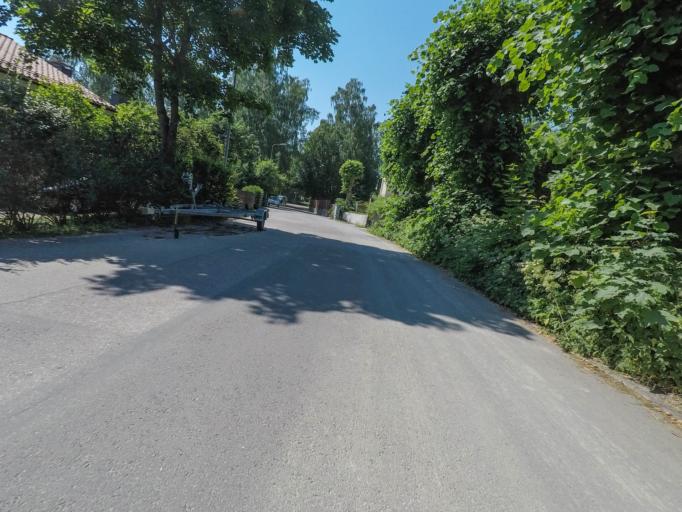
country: FI
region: Uusimaa
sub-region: Helsinki
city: Vantaa
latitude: 60.2014
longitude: 25.0852
